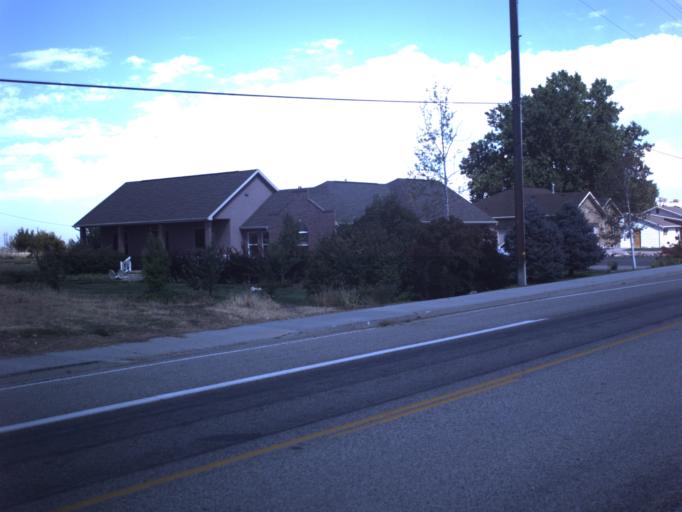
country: US
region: Utah
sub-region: Weber County
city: Farr West
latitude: 41.2827
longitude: -112.0280
